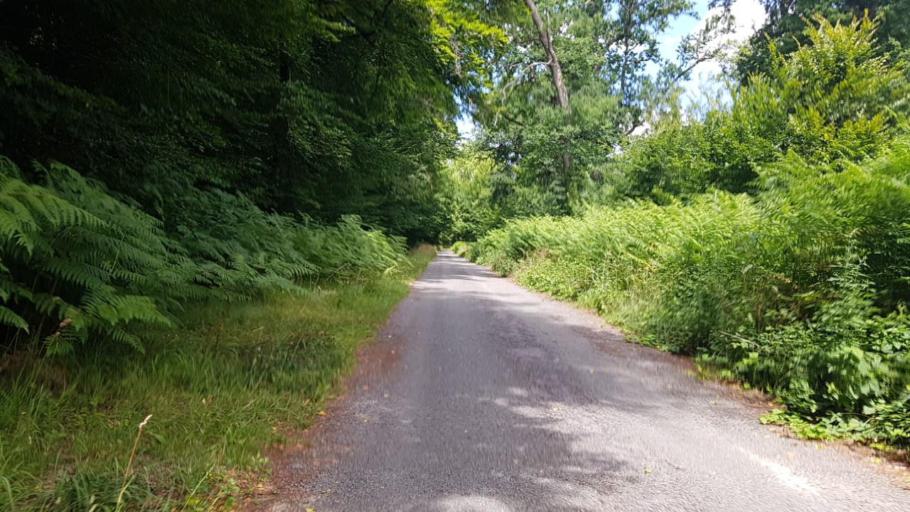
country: FR
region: Picardie
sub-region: Departement de l'Oise
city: Le Plessis-Brion
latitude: 49.4637
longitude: 2.9083
